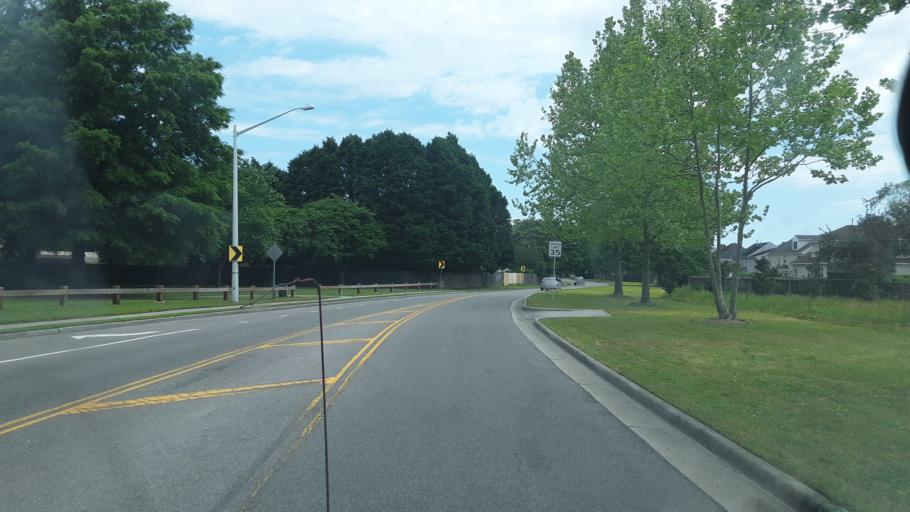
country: US
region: Virginia
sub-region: City of Virginia Beach
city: Virginia Beach
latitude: 36.7636
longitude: -76.0035
